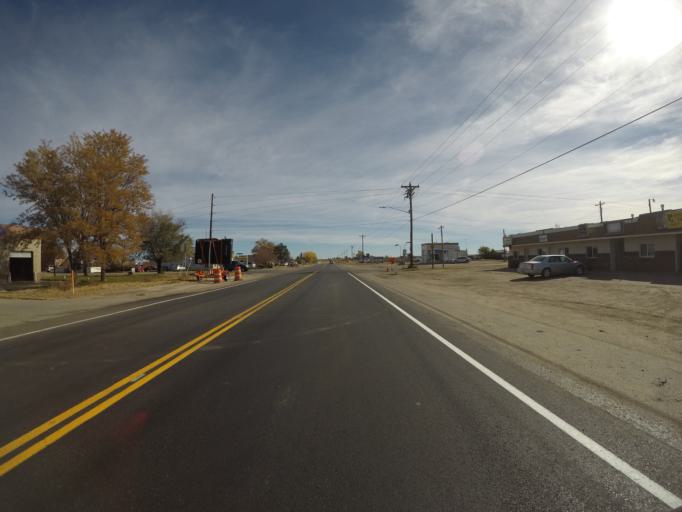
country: US
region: Colorado
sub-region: Adams County
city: Strasburg
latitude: 39.7384
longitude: -104.3220
